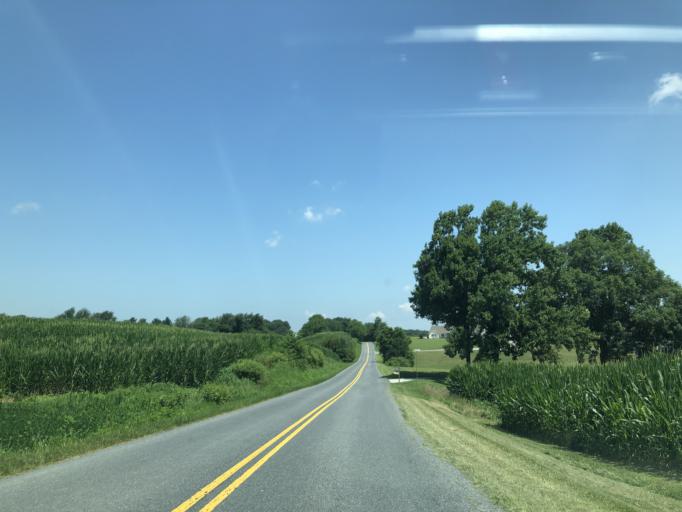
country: US
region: Maryland
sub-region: Carroll County
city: Westminster
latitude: 39.5238
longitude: -76.9877
